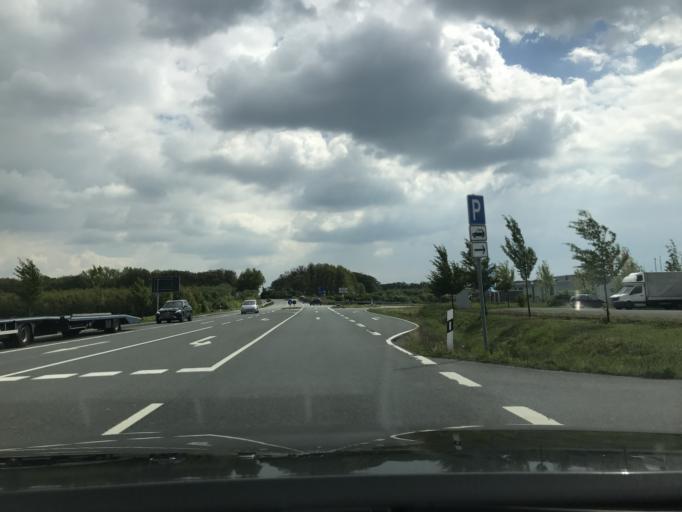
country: DE
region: North Rhine-Westphalia
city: Oelde
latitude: 51.8329
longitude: 8.2203
